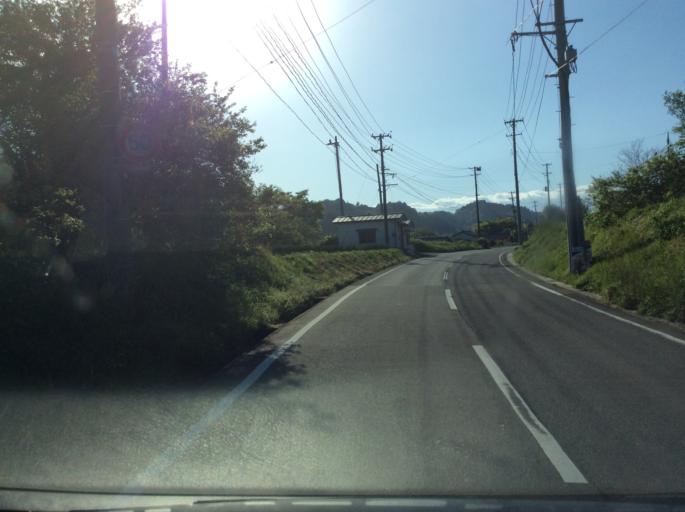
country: JP
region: Fukushima
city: Iwaki
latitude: 36.9860
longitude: 140.8345
